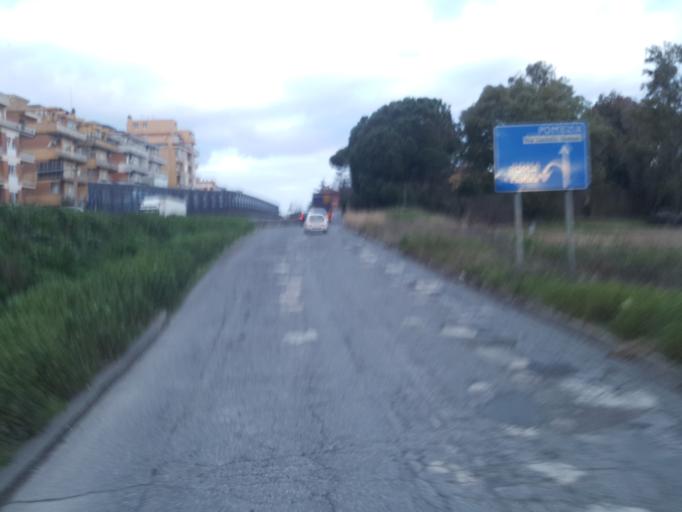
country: IT
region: Latium
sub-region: Citta metropolitana di Roma Capitale
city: Area Produttiva
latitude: 41.6743
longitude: 12.5029
